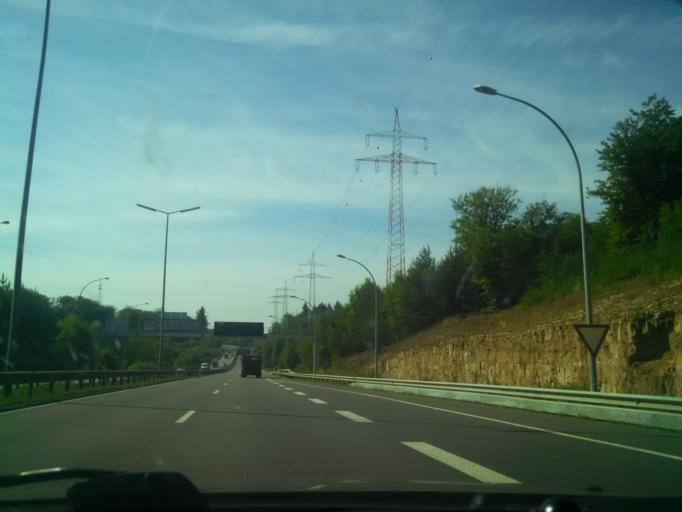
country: LU
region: Luxembourg
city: Kirchberg
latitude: 49.6483
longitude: 6.1866
